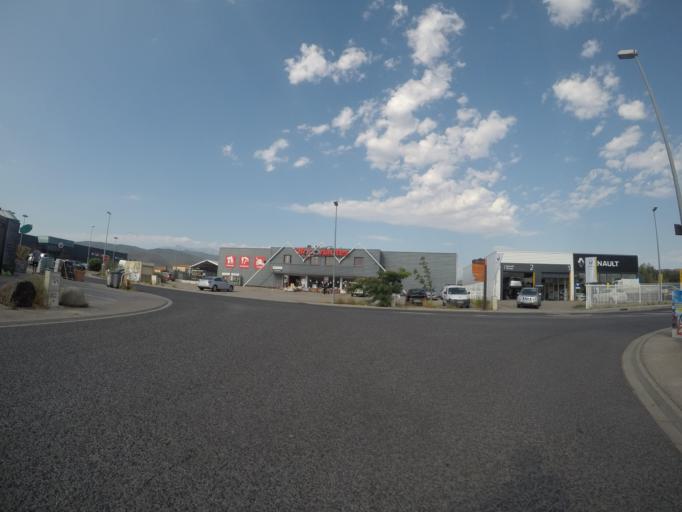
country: FR
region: Languedoc-Roussillon
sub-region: Departement des Pyrenees-Orientales
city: Ille-sur-Tet
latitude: 42.6772
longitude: 2.6333
